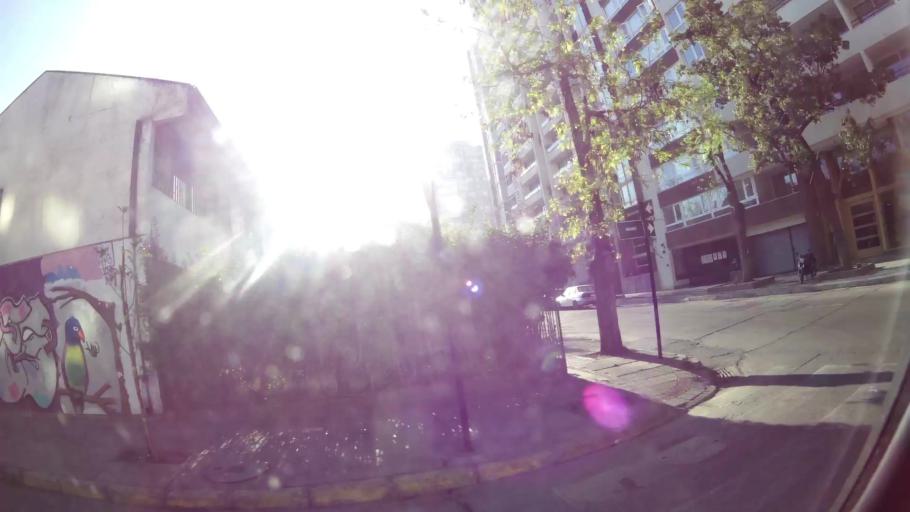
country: CL
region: Santiago Metropolitan
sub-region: Provincia de Santiago
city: Santiago
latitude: -33.4477
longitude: -70.6382
